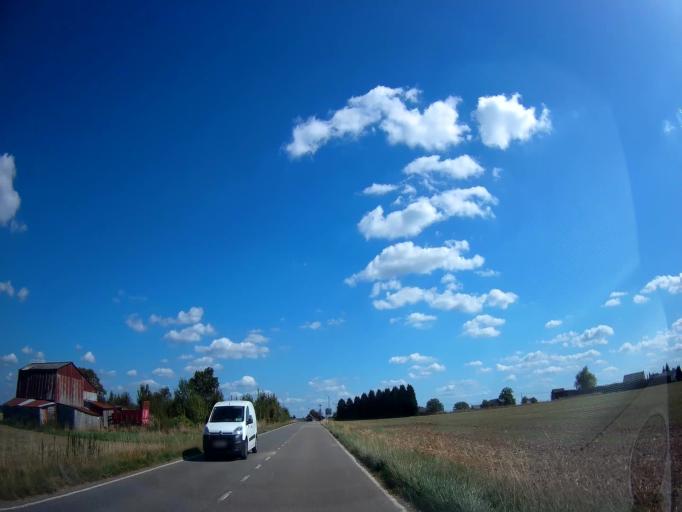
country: FR
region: Champagne-Ardenne
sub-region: Departement des Ardennes
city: Fromelennes
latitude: 50.1718
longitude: 4.8772
